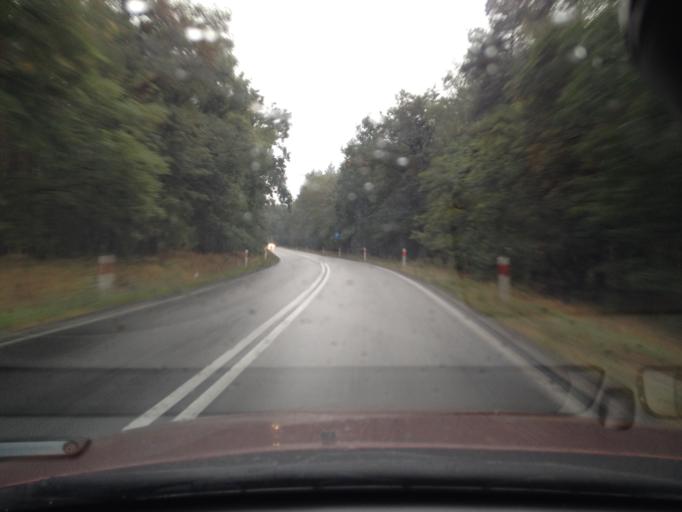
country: PL
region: Lubusz
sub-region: Powiat zaganski
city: Ilowa
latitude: 51.5411
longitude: 15.2470
